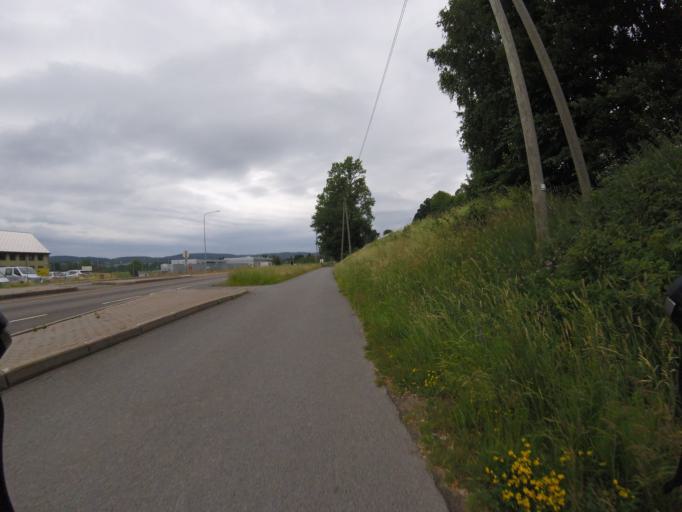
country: NO
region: Akershus
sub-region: Skedsmo
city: Lillestrom
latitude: 59.9746
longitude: 11.0333
